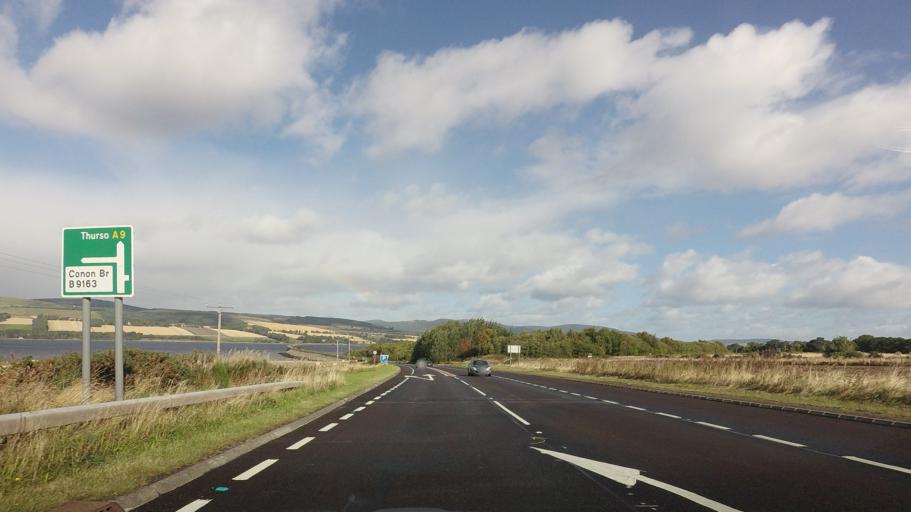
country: GB
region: Scotland
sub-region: Highland
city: Evanton
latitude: 57.6072
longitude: -4.3530
